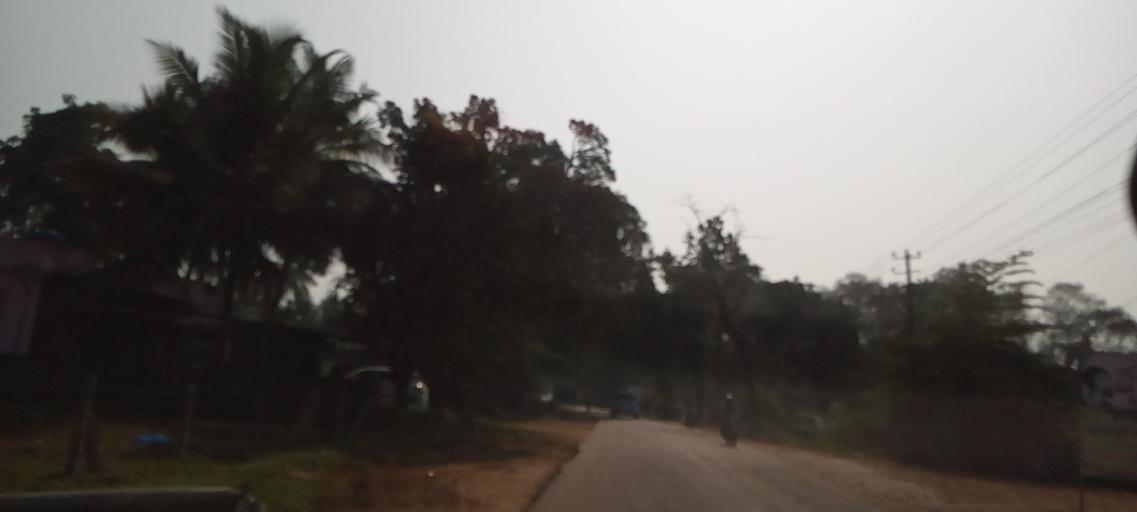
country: IN
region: Karnataka
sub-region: Udupi
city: Coondapoor
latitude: 13.5123
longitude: 74.7744
